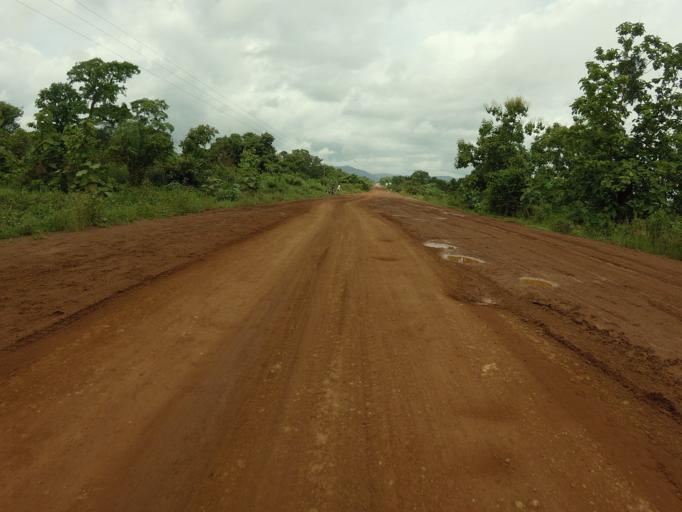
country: GH
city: Kpandae
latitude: 8.2799
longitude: 0.5061
